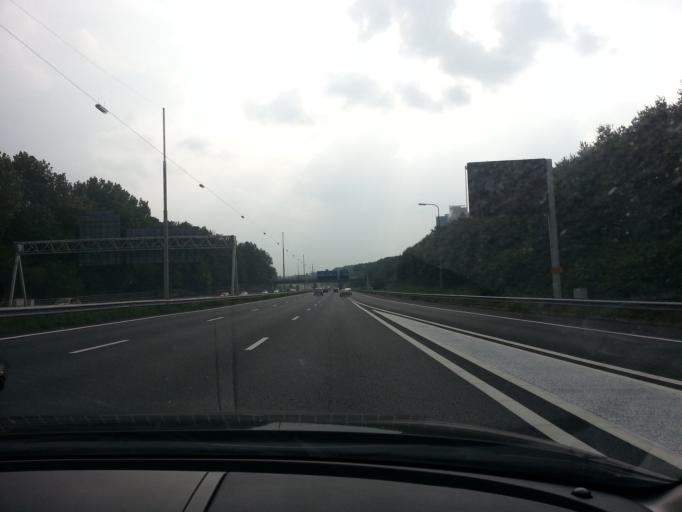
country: NL
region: South Holland
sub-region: Gemeente Rijswijk
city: Rijswijk
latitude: 52.0355
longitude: 4.3347
